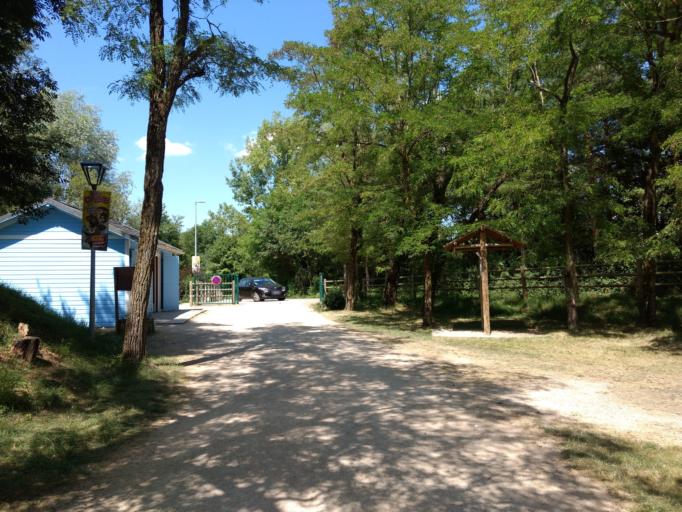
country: FR
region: Midi-Pyrenees
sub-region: Departement de l'Aveyron
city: Severac-le-Chateau
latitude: 44.3263
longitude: 3.0457
